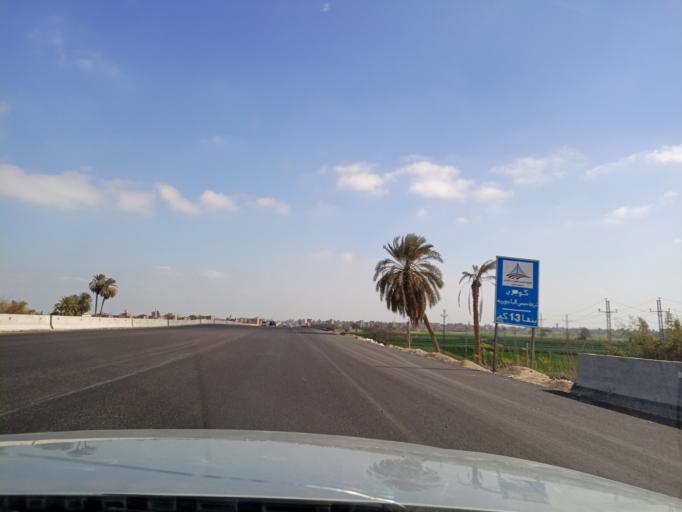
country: EG
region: Muhafazat al Minufiyah
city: Al Bajur
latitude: 30.4124
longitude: 31.0600
